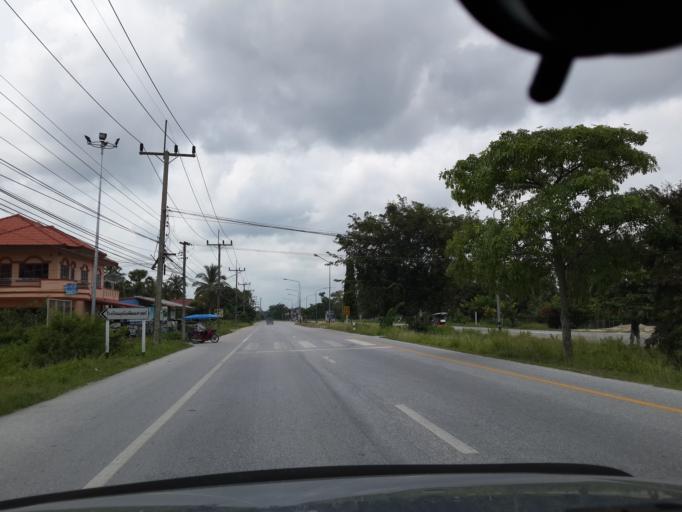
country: TH
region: Pattani
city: Yaring
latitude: 6.8694
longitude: 101.3494
